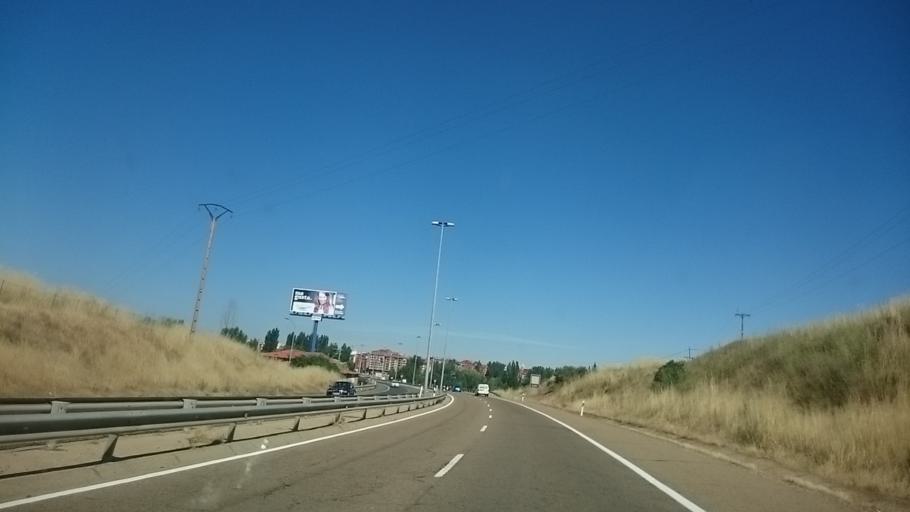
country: ES
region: Castille and Leon
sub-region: Provincia de Leon
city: Leon
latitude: 42.5842
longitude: -5.5485
